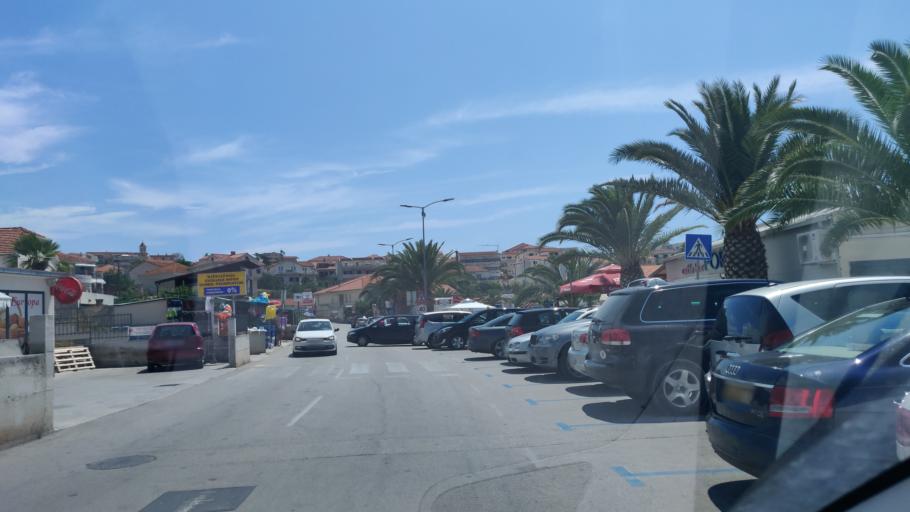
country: HR
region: Splitsko-Dalmatinska
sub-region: Grad Trogir
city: Trogir
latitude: 43.4969
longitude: 16.2605
